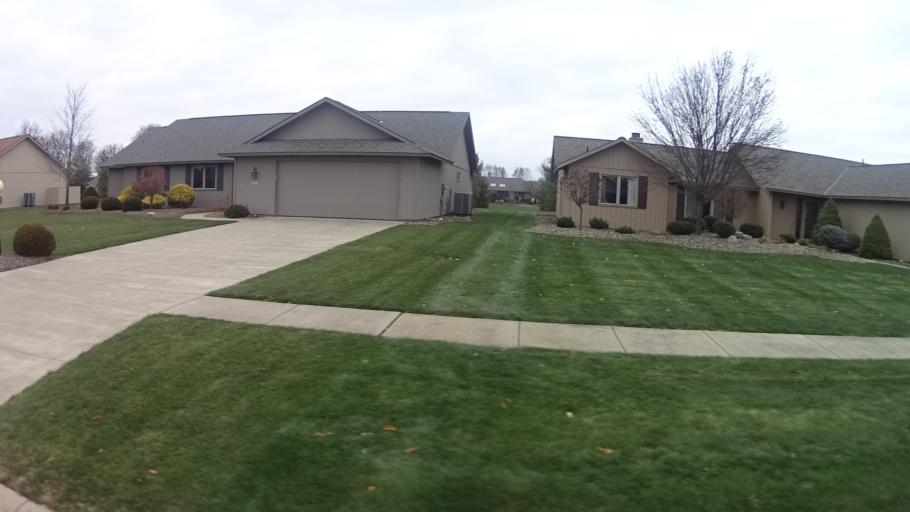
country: US
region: Ohio
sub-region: Lorain County
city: North Ridgeville
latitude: 41.3620
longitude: -81.9841
